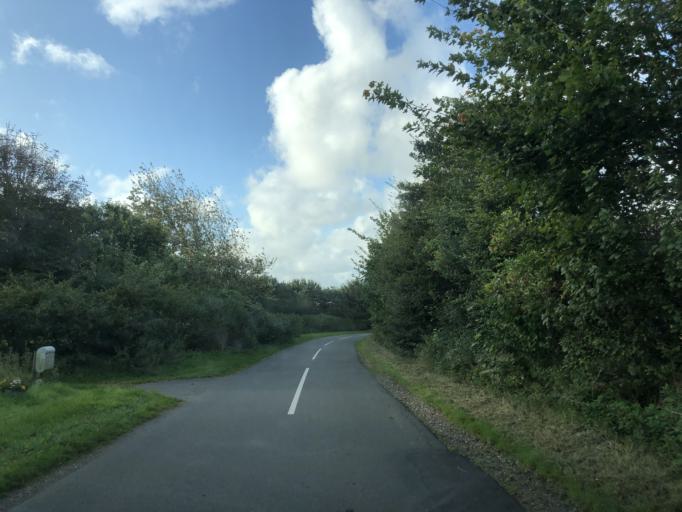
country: DK
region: Central Jutland
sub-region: Holstebro Kommune
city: Ulfborg
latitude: 56.3878
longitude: 8.3497
